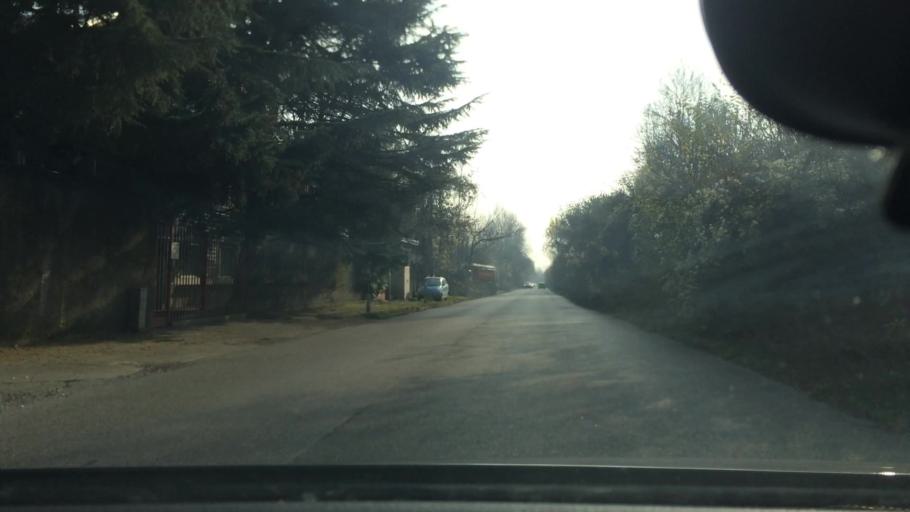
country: IT
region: Lombardy
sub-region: Provincia di Monza e Brianza
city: Villaggio del Sole
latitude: 45.6044
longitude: 9.0954
